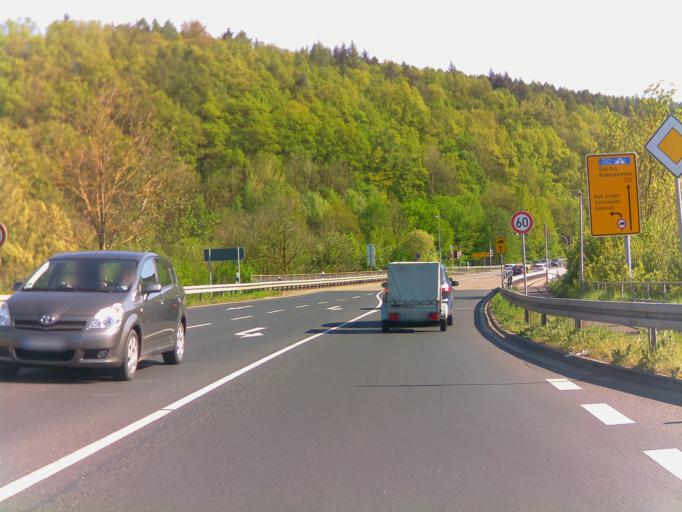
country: DE
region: Hesse
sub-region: Regierungsbezirk Darmstadt
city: Wachtersbach
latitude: 50.2543
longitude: 9.3015
